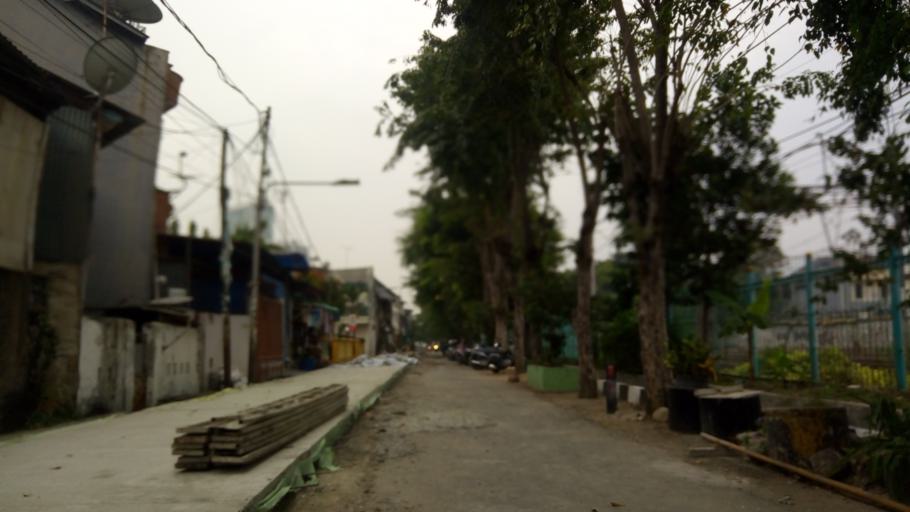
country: ID
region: Jakarta Raya
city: Jakarta
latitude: -6.1535
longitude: 106.8391
